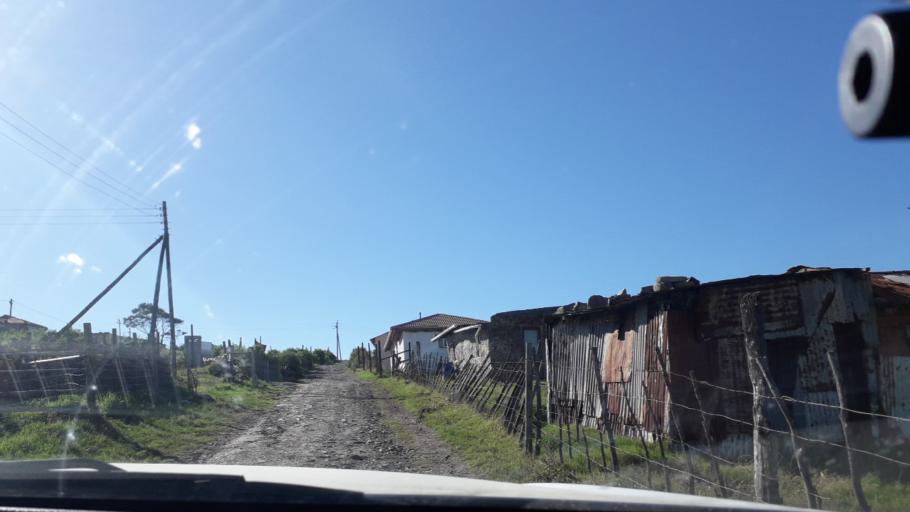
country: ZA
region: Eastern Cape
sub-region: Buffalo City Metropolitan Municipality
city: East London
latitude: -32.8455
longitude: 27.9856
